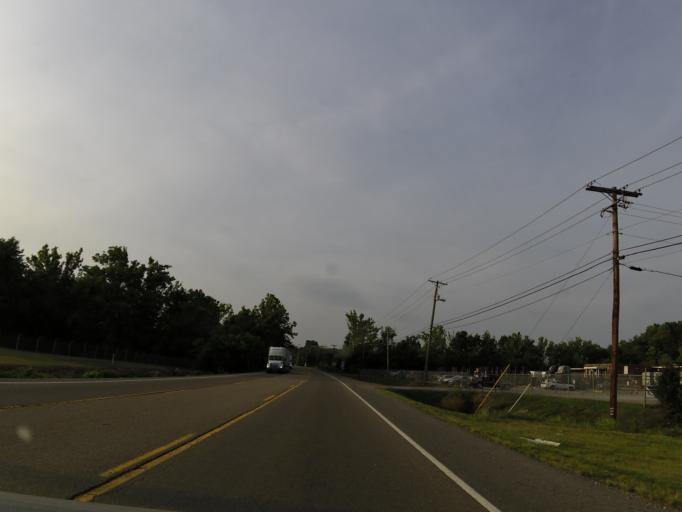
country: US
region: Tennessee
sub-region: Knox County
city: Knoxville
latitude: 35.9769
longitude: -83.8258
